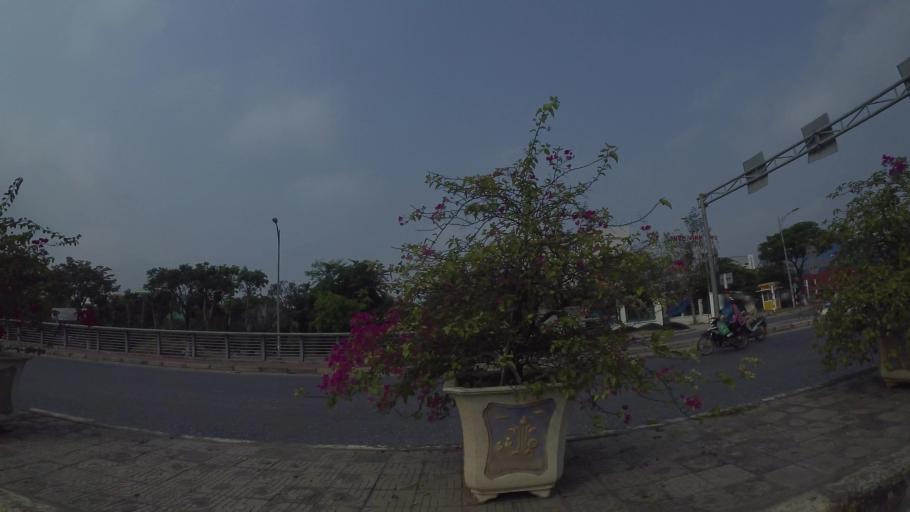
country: VN
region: Da Nang
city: Cam Le
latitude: 16.0197
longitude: 108.2114
